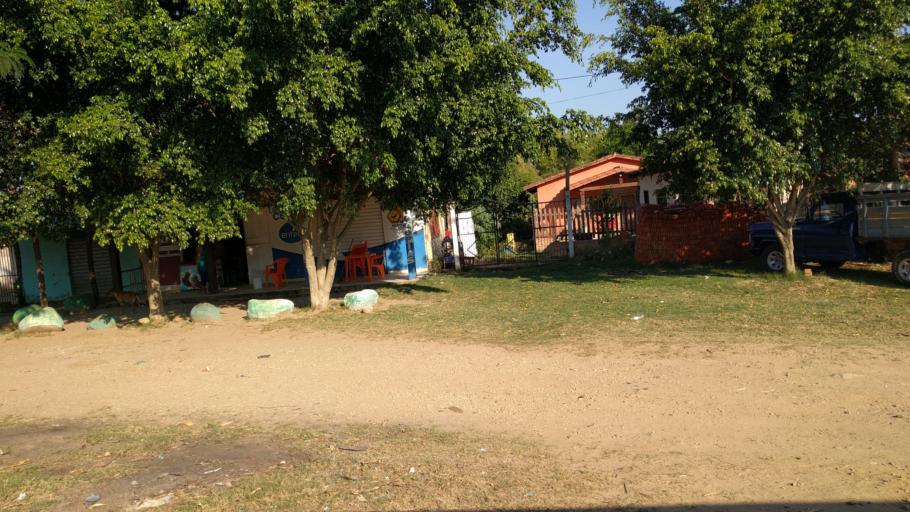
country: BO
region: Santa Cruz
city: Jorochito
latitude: -18.1426
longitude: -63.4804
